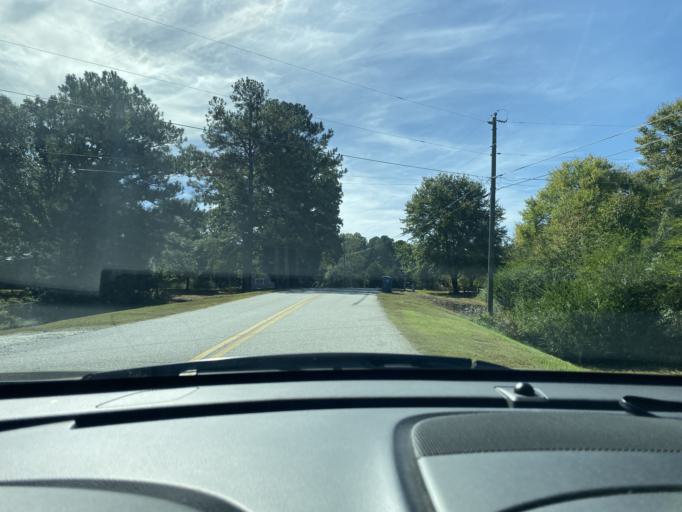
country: US
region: Georgia
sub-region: Walton County
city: Loganville
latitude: 33.8731
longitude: -83.9044
